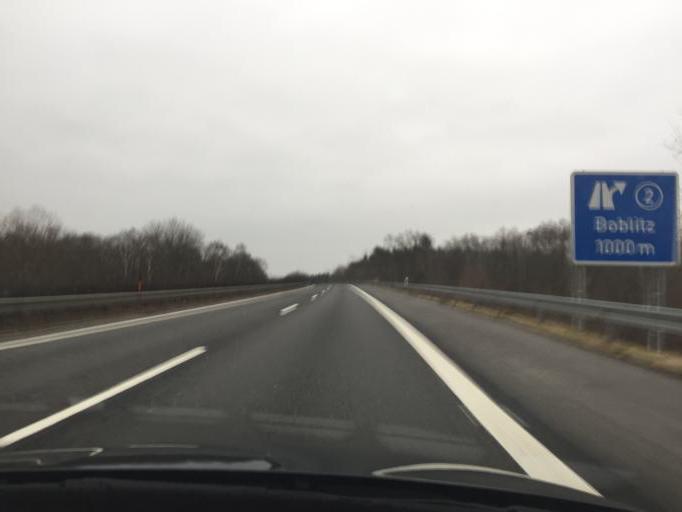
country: DE
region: Brandenburg
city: Lubbenau
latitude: 51.8373
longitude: 13.9620
